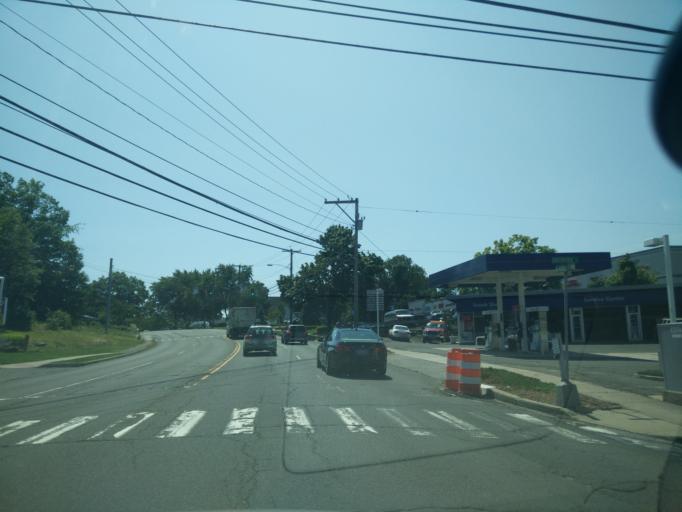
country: US
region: Connecticut
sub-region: Fairfield County
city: Fairfield
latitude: 41.1840
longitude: -73.2559
